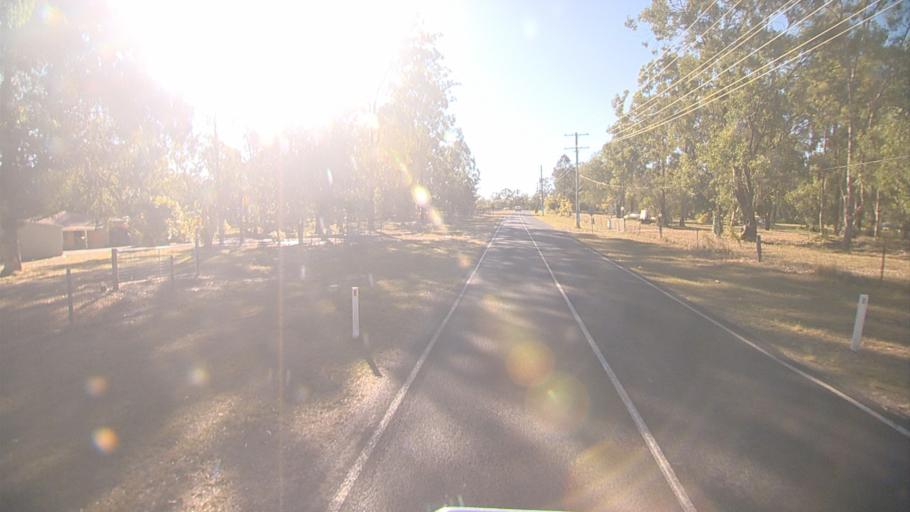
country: AU
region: Queensland
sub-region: Logan
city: Park Ridge South
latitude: -27.7406
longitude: 153.0178
